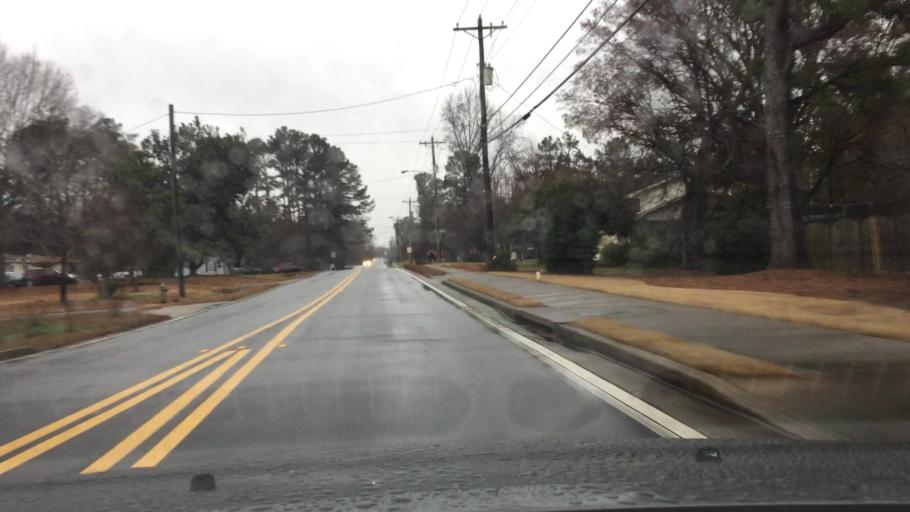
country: US
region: Georgia
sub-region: Cobb County
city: Fair Oaks
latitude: 33.9151
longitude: -84.5759
